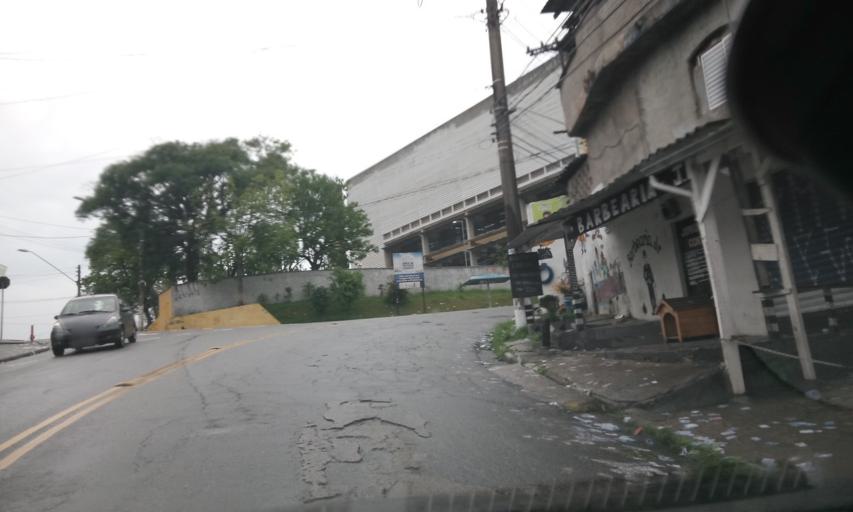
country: BR
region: Sao Paulo
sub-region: Maua
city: Maua
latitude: -23.7413
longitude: -46.4942
